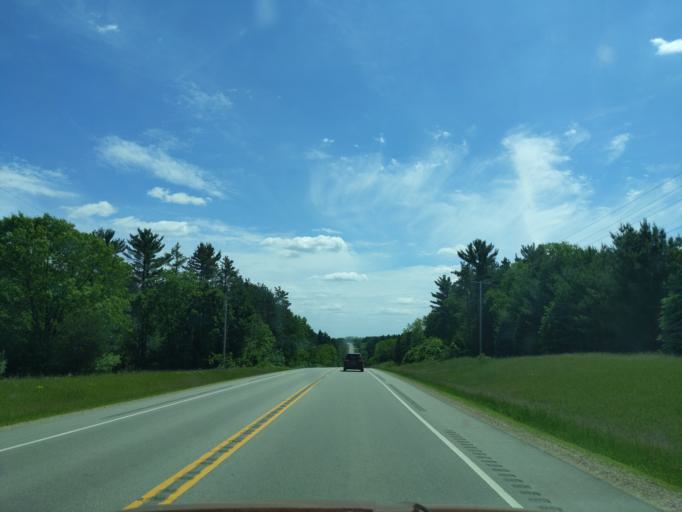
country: US
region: Wisconsin
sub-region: Columbia County
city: Pardeeville
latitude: 43.4570
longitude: -89.3252
